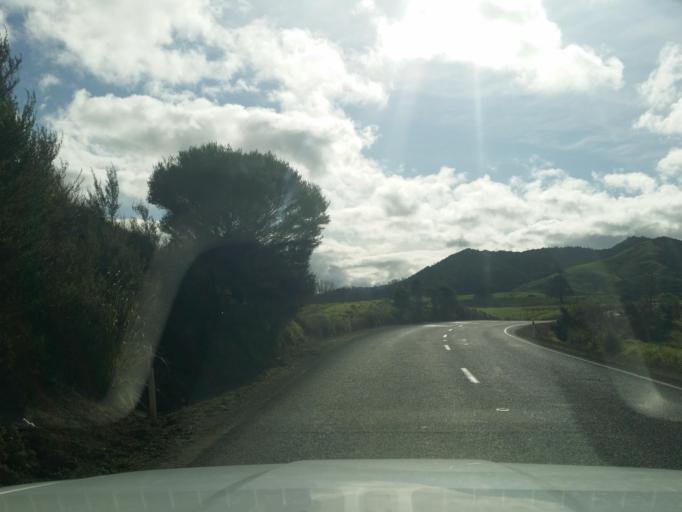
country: NZ
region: Northland
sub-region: Kaipara District
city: Dargaville
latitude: -35.8008
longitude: 173.9179
